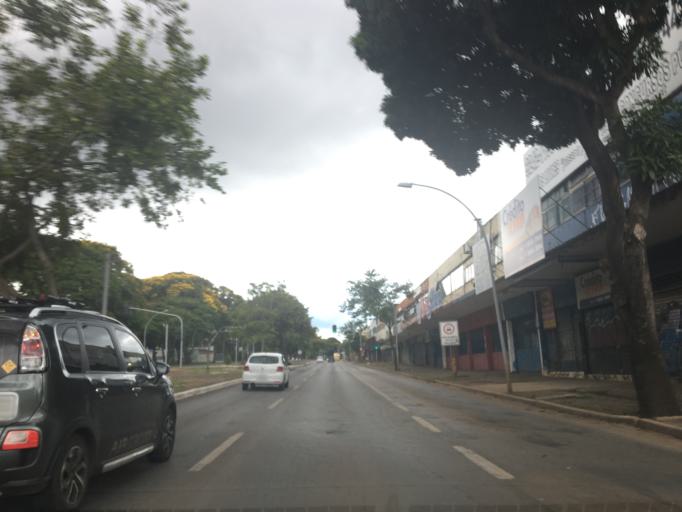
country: BR
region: Federal District
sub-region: Brasilia
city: Brasilia
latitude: -15.8137
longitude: -47.9079
